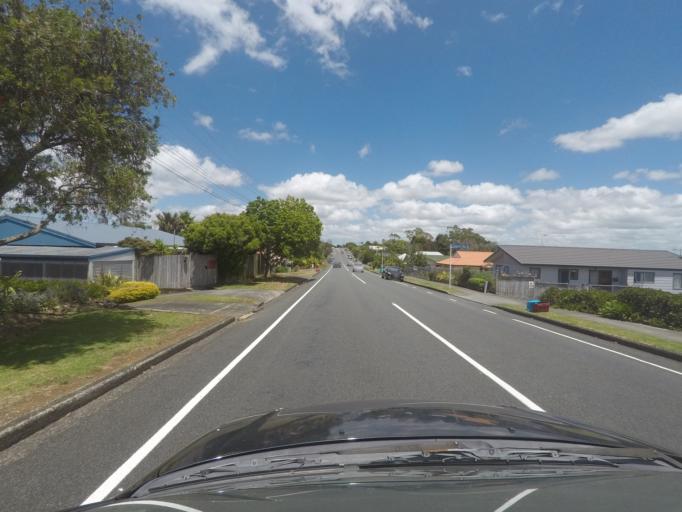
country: NZ
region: Northland
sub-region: Whangarei
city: Whangarei
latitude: -35.7609
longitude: 174.3671
